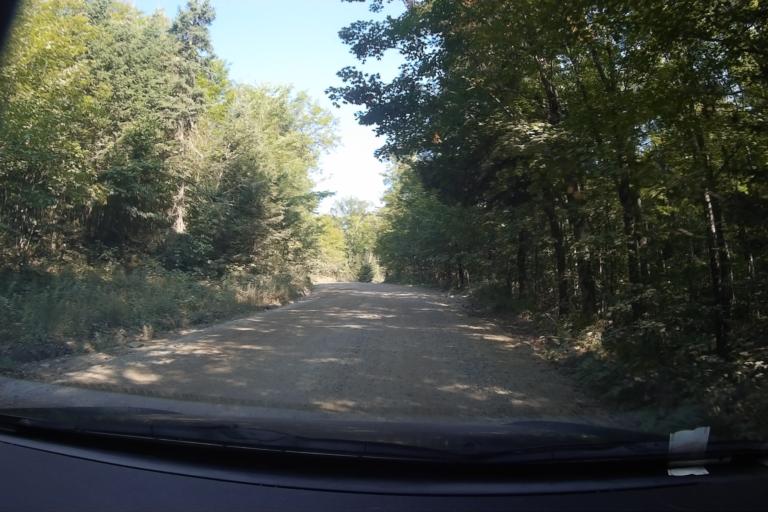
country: CA
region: Ontario
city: Huntsville
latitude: 45.5491
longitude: -78.6958
